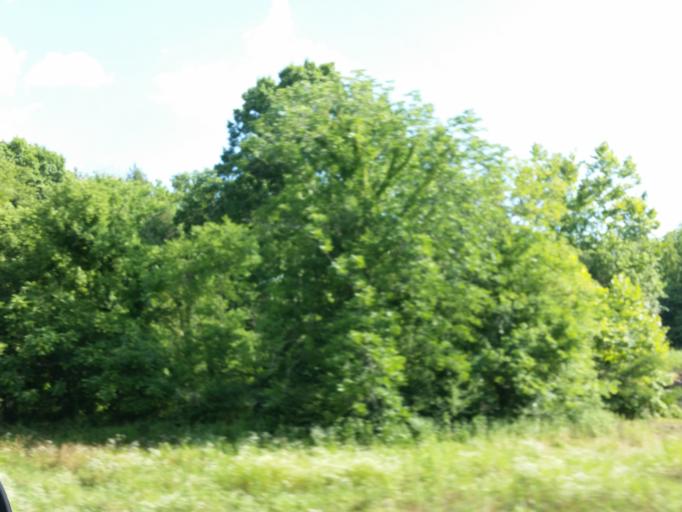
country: US
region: Tennessee
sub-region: Perry County
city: Linden
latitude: 35.6340
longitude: -87.7775
